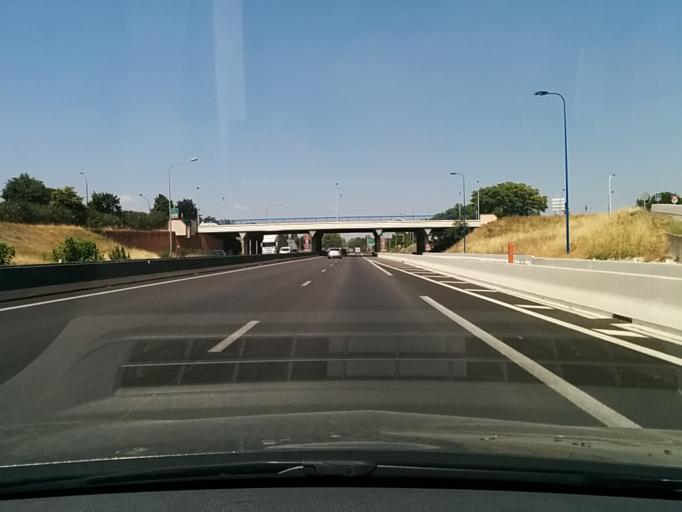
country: FR
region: Midi-Pyrenees
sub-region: Departement de la Haute-Garonne
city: Ramonville-Saint-Agne
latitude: 43.5709
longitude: 1.4763
